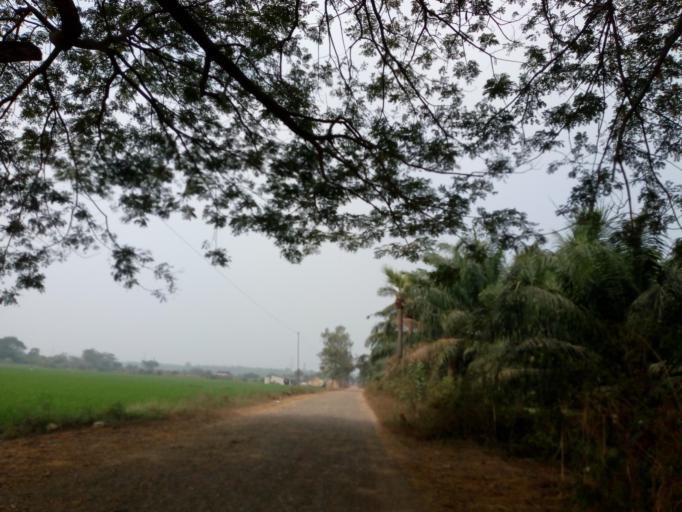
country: IN
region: Andhra Pradesh
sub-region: West Godavari
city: Tadepallegudem
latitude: 16.8662
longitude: 81.3071
